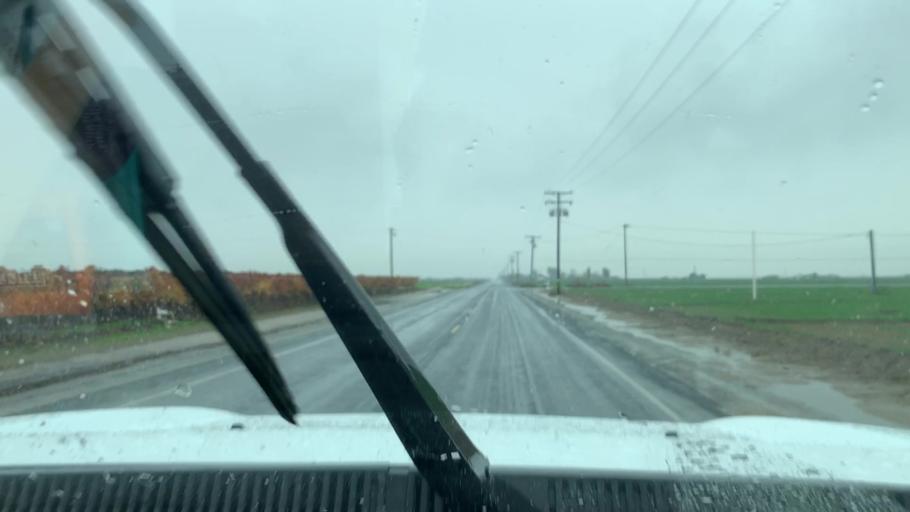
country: US
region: California
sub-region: Tulare County
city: Earlimart
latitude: 35.8919
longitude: -119.3023
